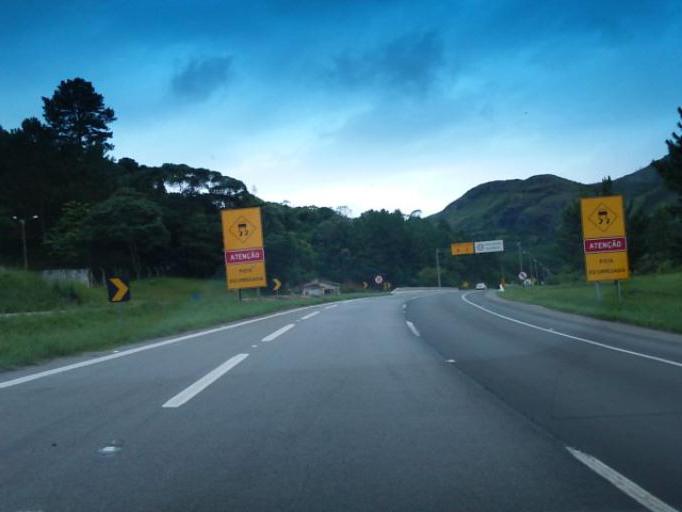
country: BR
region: Parana
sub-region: Campina Grande Do Sul
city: Campina Grande do Sul
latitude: -25.1150
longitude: -48.8518
